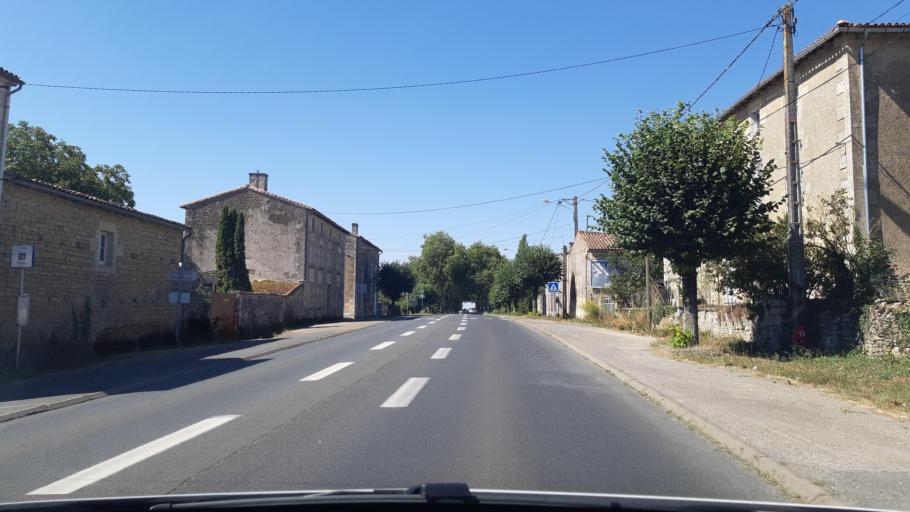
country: FR
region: Poitou-Charentes
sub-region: Departement des Deux-Sevres
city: Azay-le-Brule
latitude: 46.3913
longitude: -0.2587
